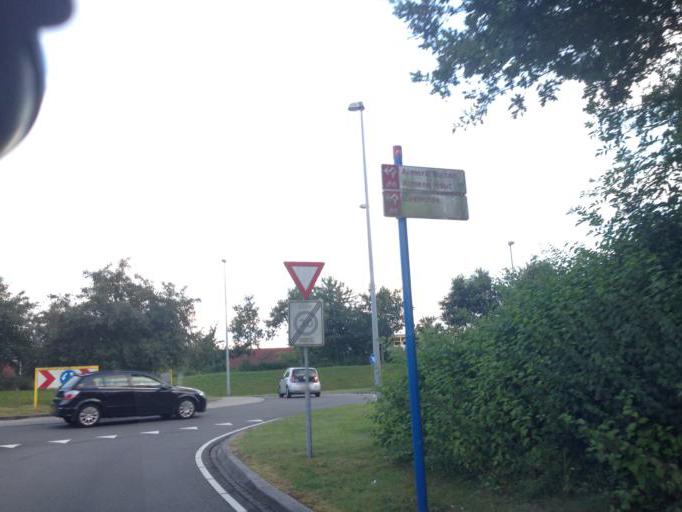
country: NL
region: Flevoland
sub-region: Gemeente Almere
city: Almere Stad
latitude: 52.3690
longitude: 5.2559
